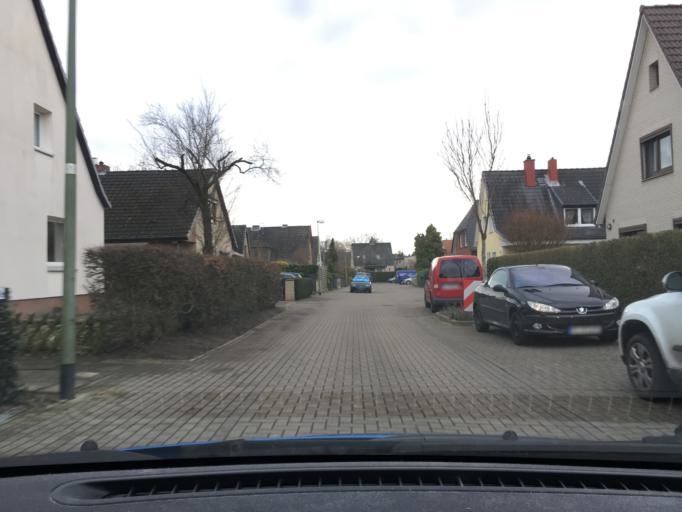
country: DE
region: Schleswig-Holstein
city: Wedel
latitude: 53.5784
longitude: 9.7161
